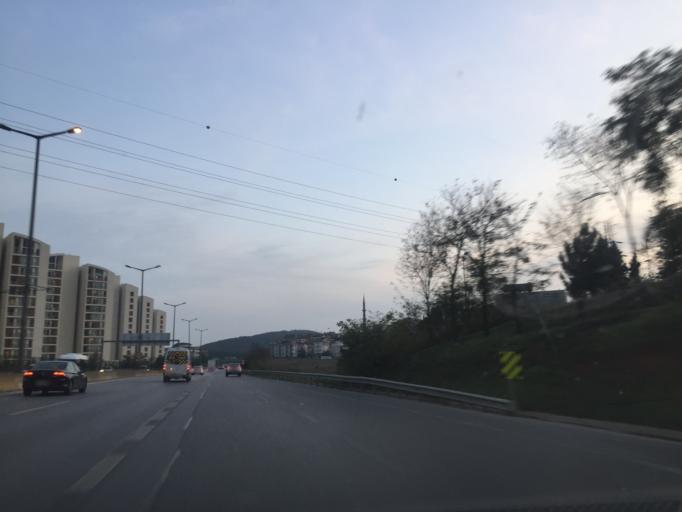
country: TR
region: Istanbul
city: Samandira
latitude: 40.9663
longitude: 29.2188
